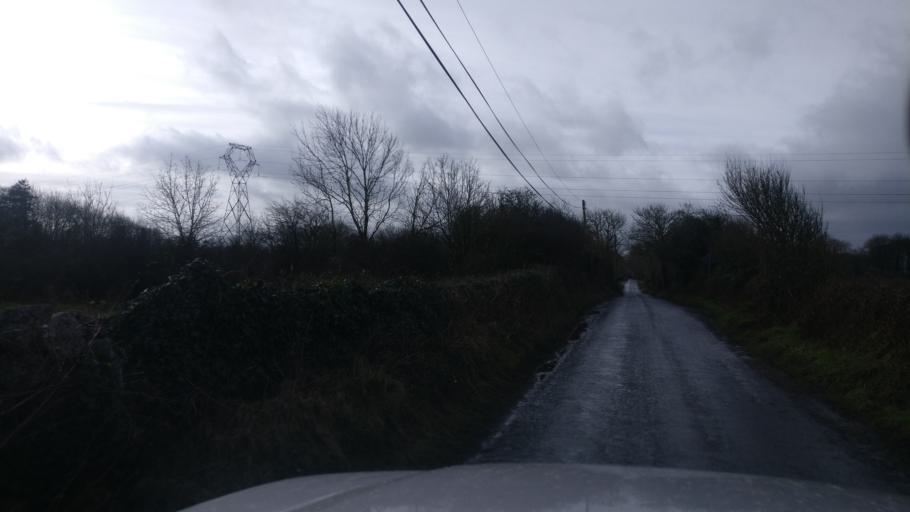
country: IE
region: Connaught
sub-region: County Galway
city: Athenry
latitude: 53.2763
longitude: -8.7666
